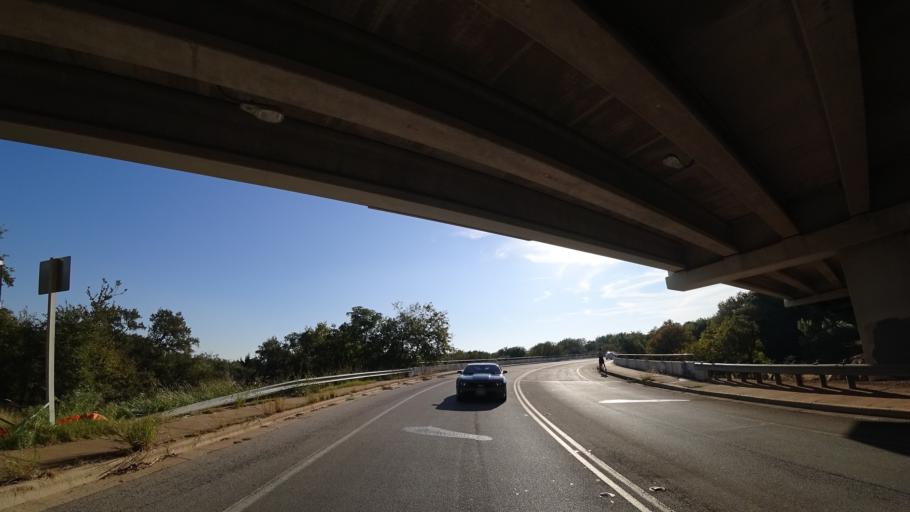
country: US
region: Texas
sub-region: Travis County
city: Shady Hollow
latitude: 30.2164
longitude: -97.8462
